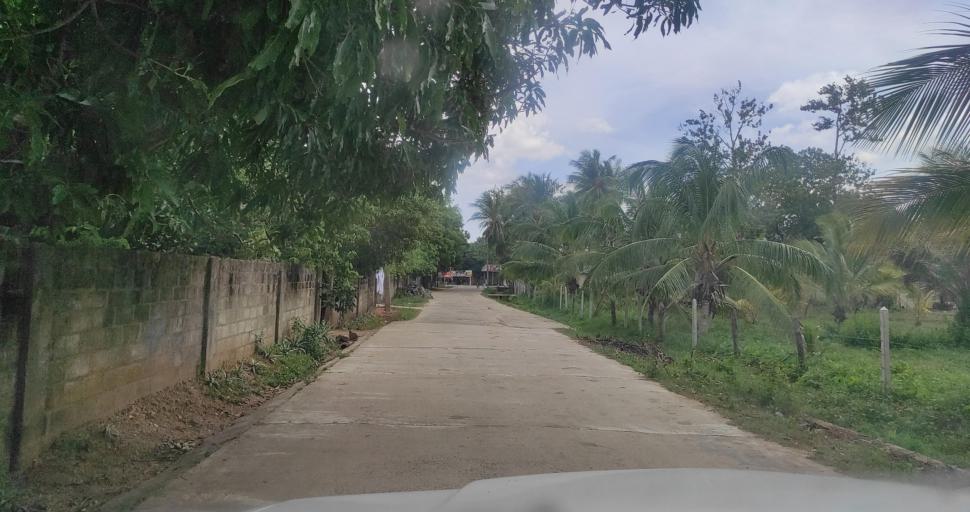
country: LK
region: Eastern Province
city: Trincomalee
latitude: 8.4402
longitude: 81.0501
